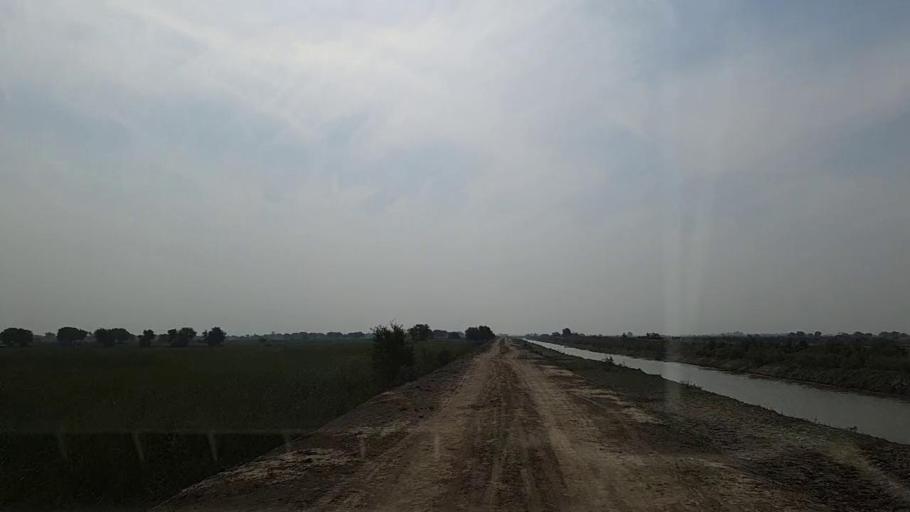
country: PK
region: Sindh
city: Mirpur Batoro
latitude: 24.6704
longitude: 68.2499
